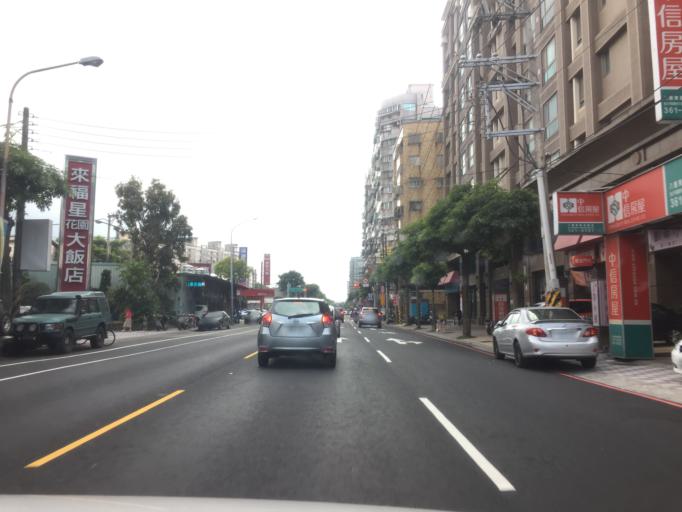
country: TW
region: Taiwan
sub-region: Taoyuan
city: Taoyuan
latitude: 24.9642
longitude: 121.3068
